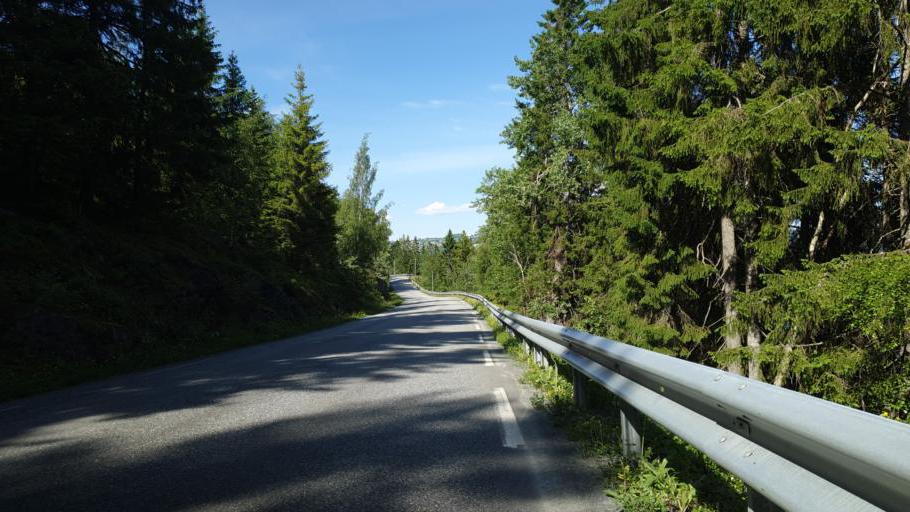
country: NO
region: Nord-Trondelag
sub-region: Leksvik
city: Leksvik
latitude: 63.6493
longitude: 10.6073
